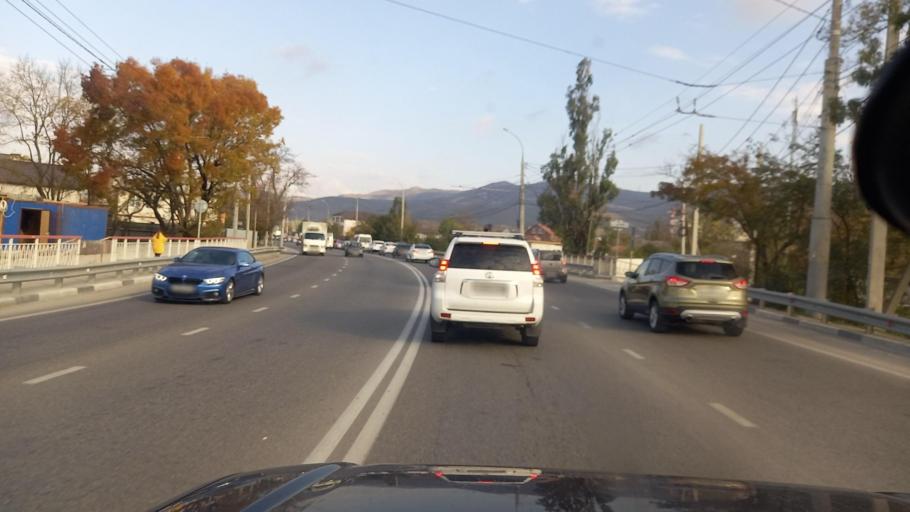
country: RU
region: Krasnodarskiy
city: Gayduk
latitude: 44.7509
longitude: 37.7275
